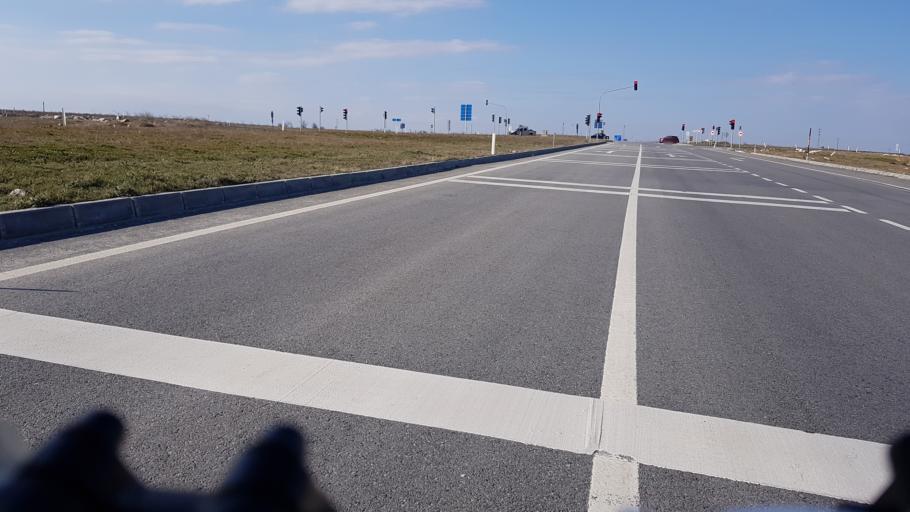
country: TR
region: Tekirdag
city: Saray
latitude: 41.4302
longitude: 27.9102
